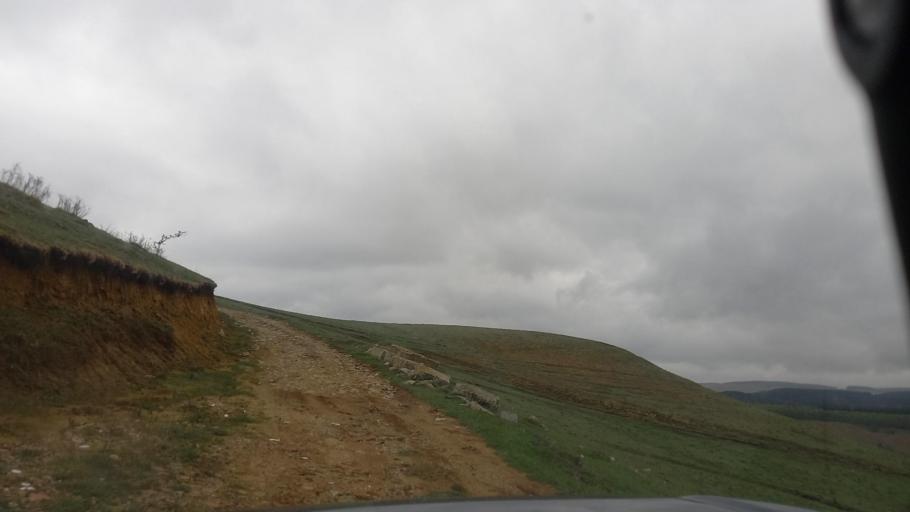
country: RU
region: Stavropol'skiy
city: Nezhinskiy
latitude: 43.8569
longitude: 42.6394
